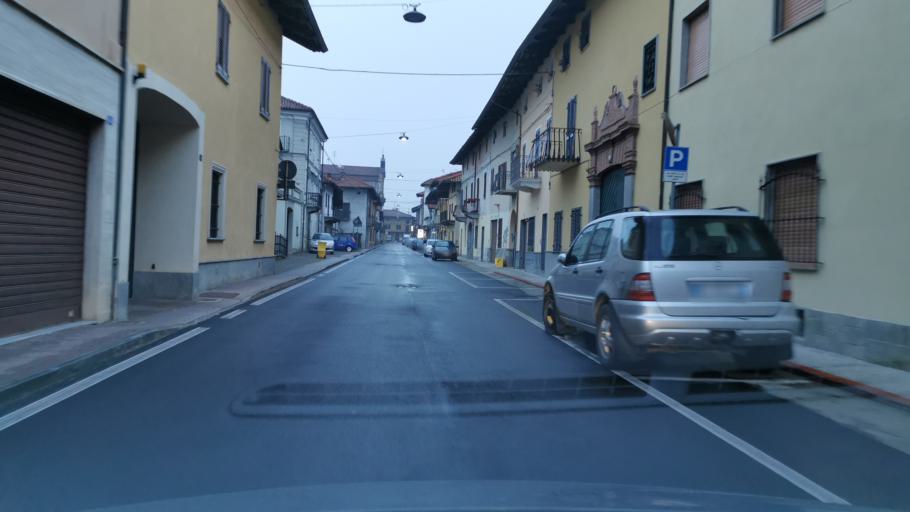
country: IT
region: Piedmont
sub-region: Provincia di Torino
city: Feletto
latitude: 45.3033
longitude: 7.7465
